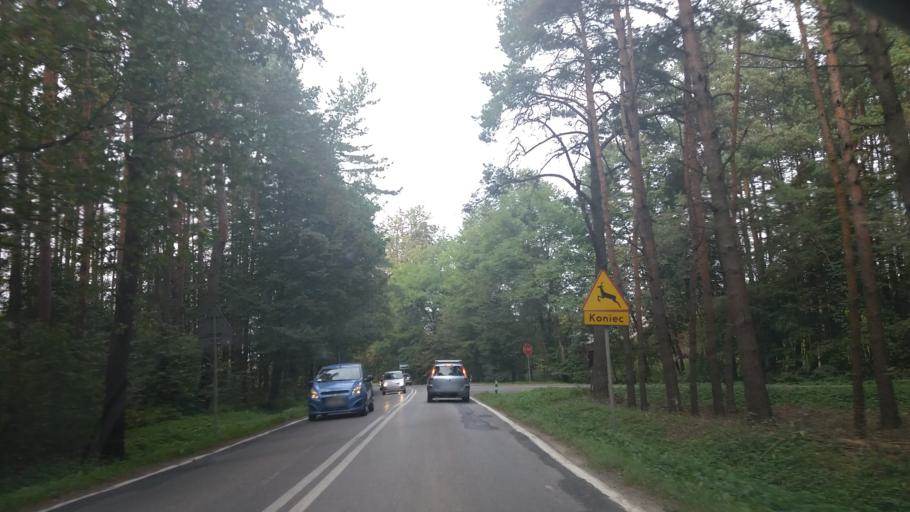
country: PL
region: Lesser Poland Voivodeship
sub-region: Powiat chrzanowski
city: Pogorzyce
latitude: 50.1229
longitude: 19.4348
